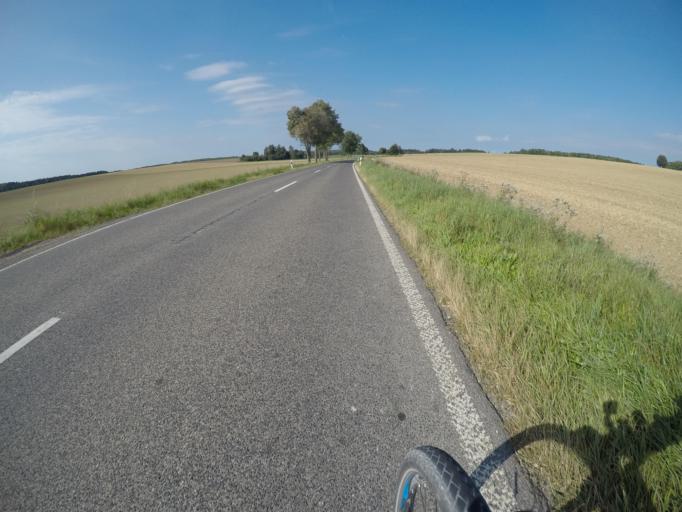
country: DE
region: Baden-Wuerttemberg
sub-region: Regierungsbezirk Stuttgart
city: Bohmenkirch
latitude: 48.6341
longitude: 9.9046
